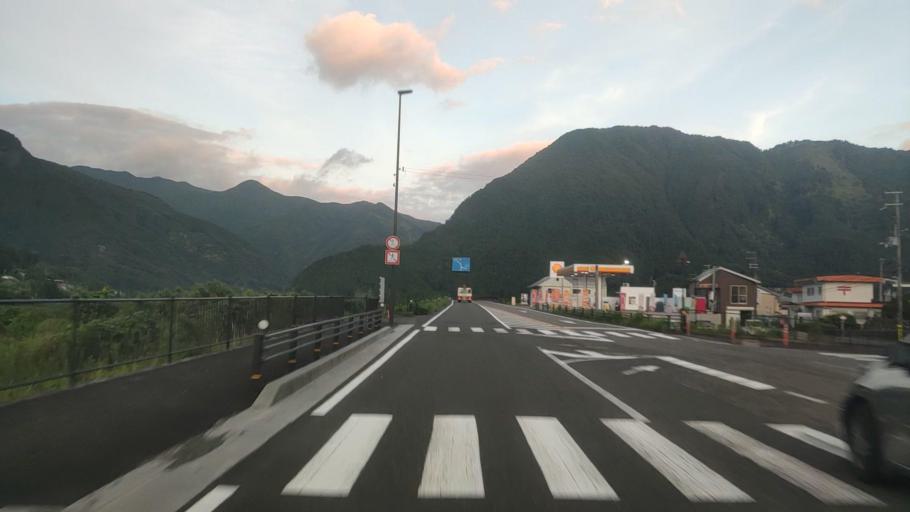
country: JP
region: Wakayama
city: Shingu
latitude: 33.8059
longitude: 135.8735
